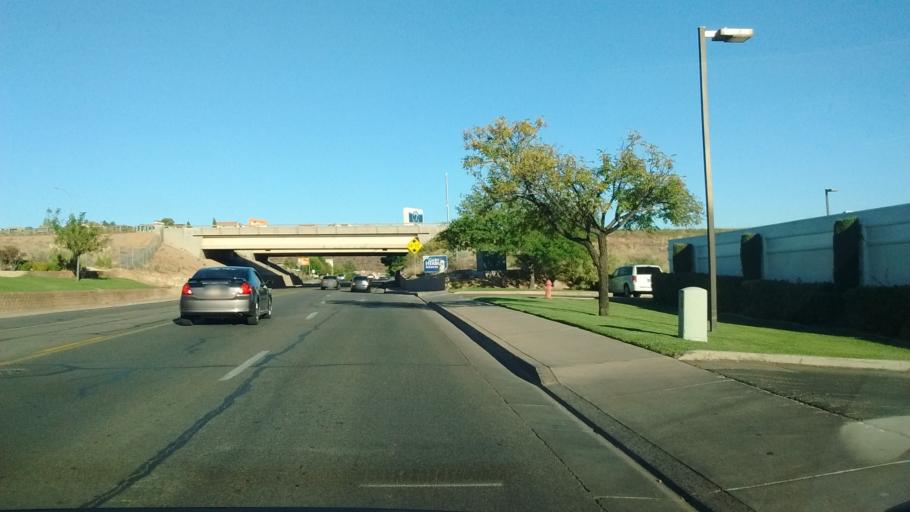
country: US
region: Utah
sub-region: Washington County
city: Saint George
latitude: 37.1064
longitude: -113.5607
